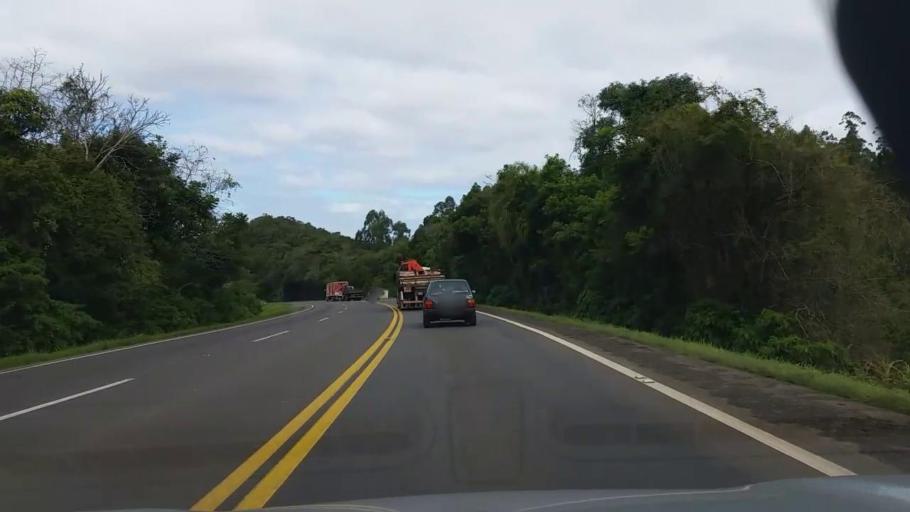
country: BR
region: Rio Grande do Sul
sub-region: Arroio Do Meio
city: Arroio do Meio
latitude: -29.3932
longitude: -52.0425
